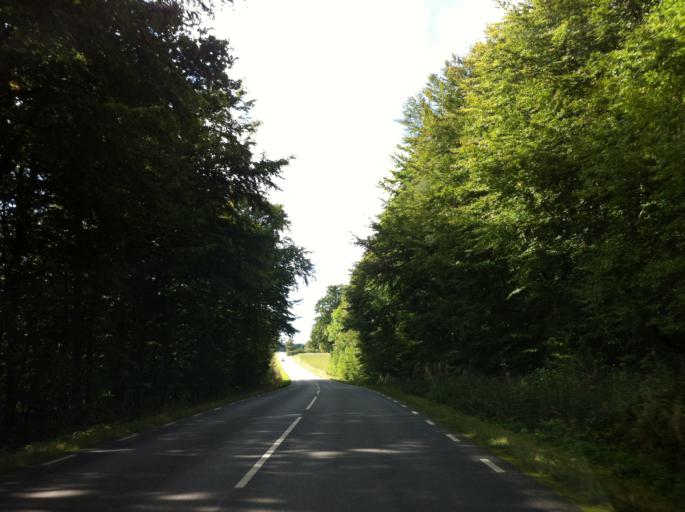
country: SE
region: Skane
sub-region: Tomelilla Kommun
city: Tomelilla
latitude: 55.6535
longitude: 13.9409
